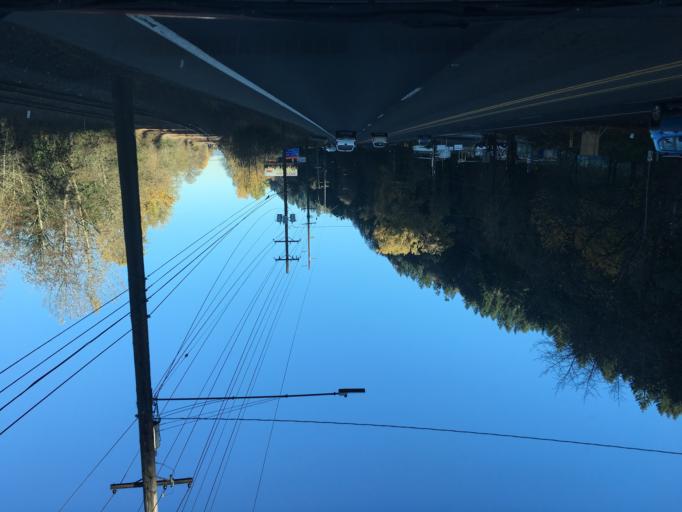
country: US
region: Oregon
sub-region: Washington County
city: West Haven
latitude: 45.5682
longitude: -122.7523
